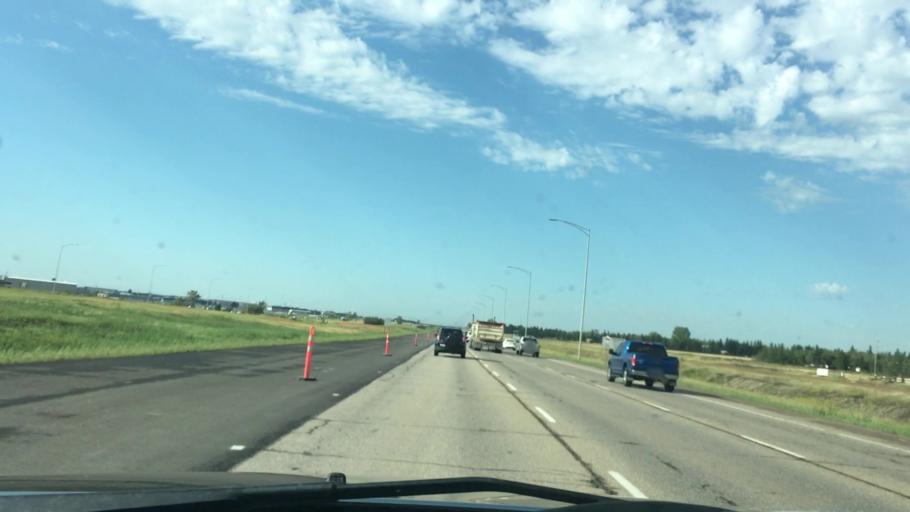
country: CA
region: Alberta
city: Beaumont
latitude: 53.3853
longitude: -113.5176
